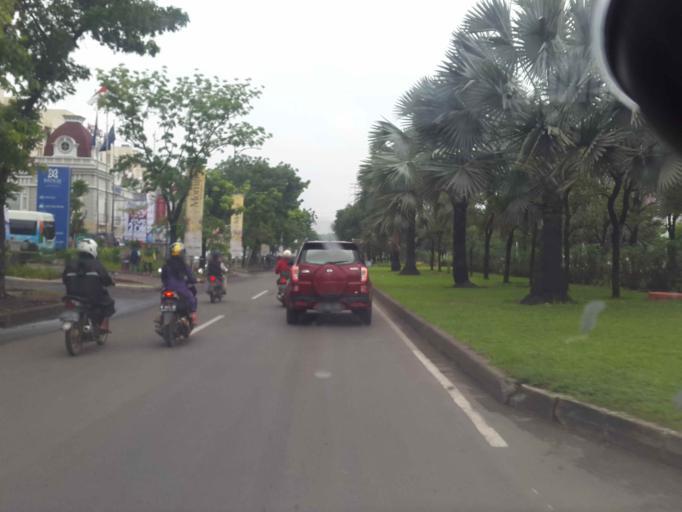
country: ID
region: West Java
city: Cikarang
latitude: -6.3003
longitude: 107.1517
